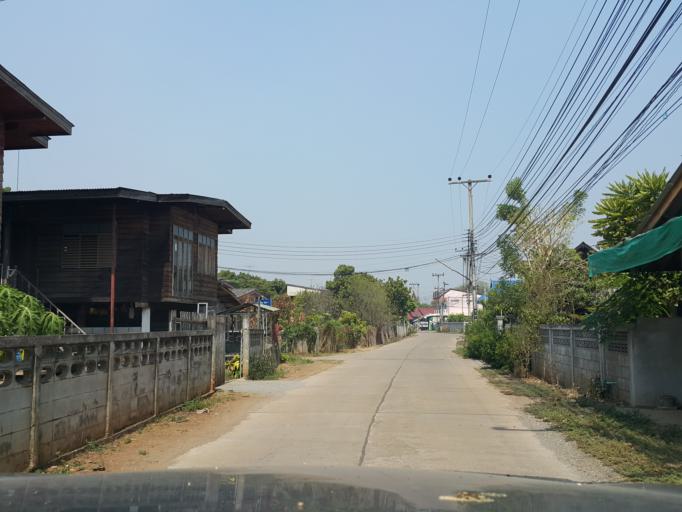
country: TH
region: Sukhothai
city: Thung Saliam
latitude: 17.3129
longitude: 99.5551
